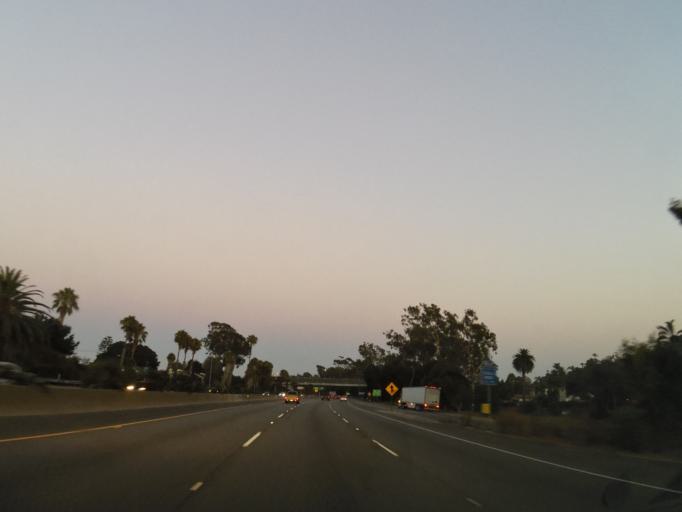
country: US
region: California
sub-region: Santa Barbara County
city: Santa Barbara
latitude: 34.4159
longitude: -119.7068
